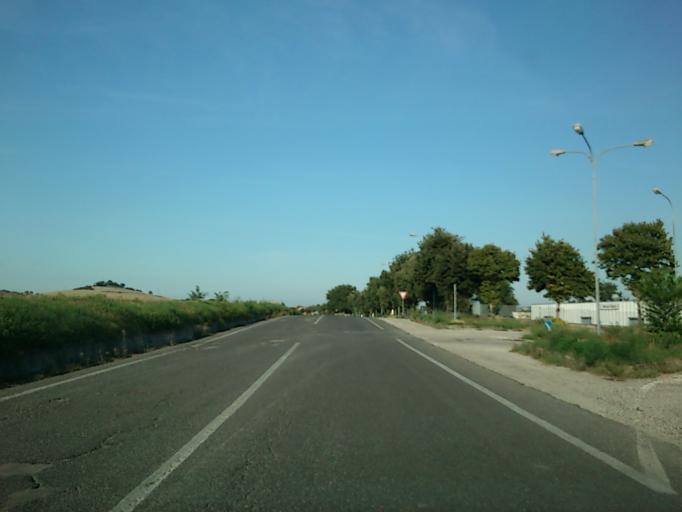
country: IT
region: The Marches
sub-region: Provincia di Pesaro e Urbino
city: Montefelcino
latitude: 43.7066
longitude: 12.8410
